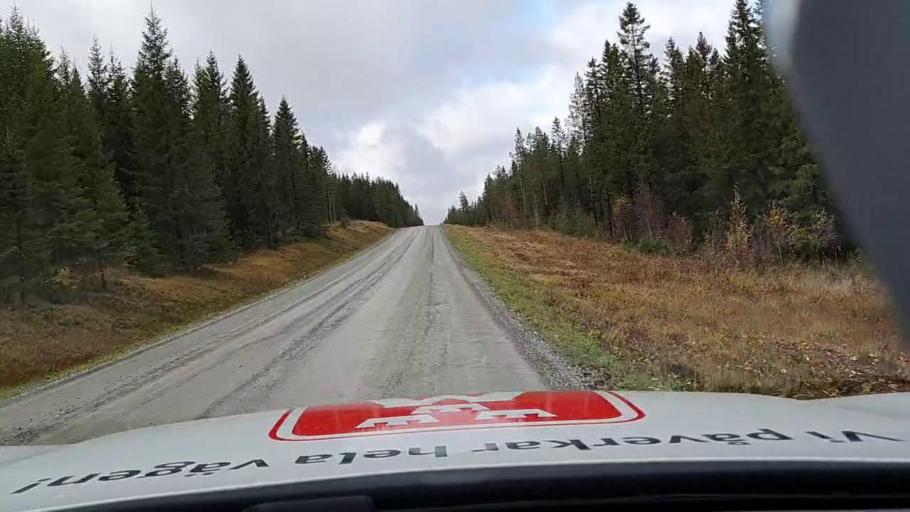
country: SE
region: Jaemtland
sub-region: Bergs Kommun
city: Hoverberg
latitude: 63.0072
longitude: 14.1240
